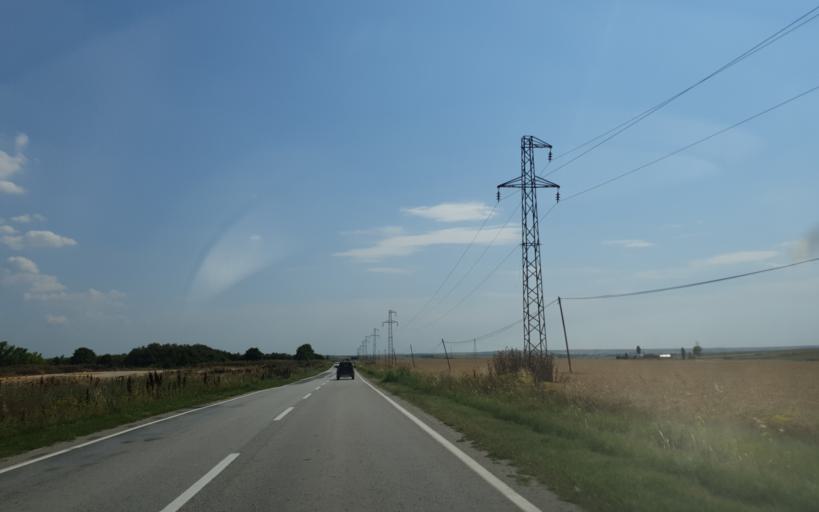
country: TR
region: Kirklareli
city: Buyukkaristiran
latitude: 41.3155
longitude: 27.5196
